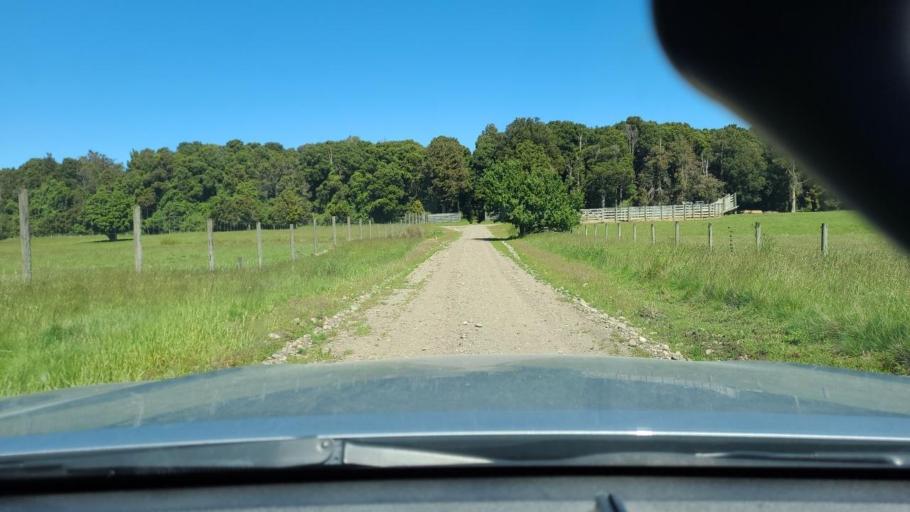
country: NZ
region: Southland
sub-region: Southland District
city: Riverton
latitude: -45.9535
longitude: 167.6847
